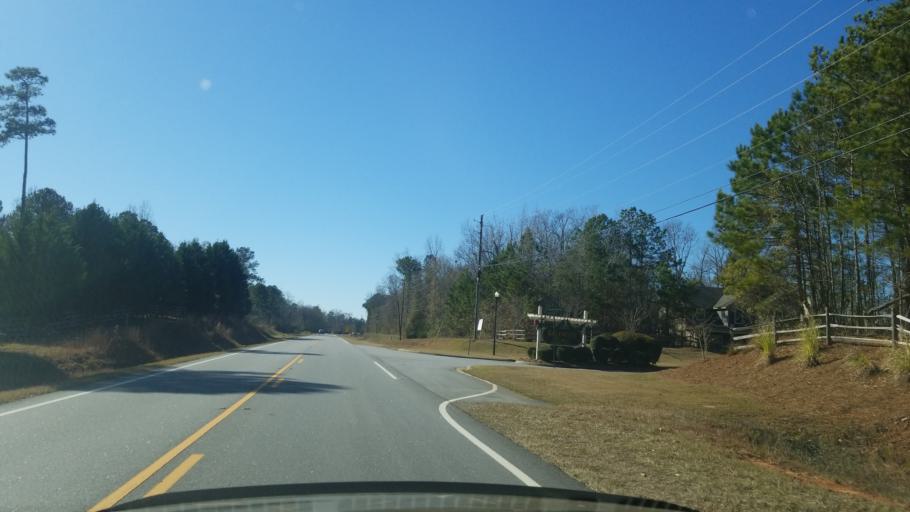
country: US
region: Georgia
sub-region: Harris County
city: Hamilton
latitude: 32.6311
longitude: -84.7651
